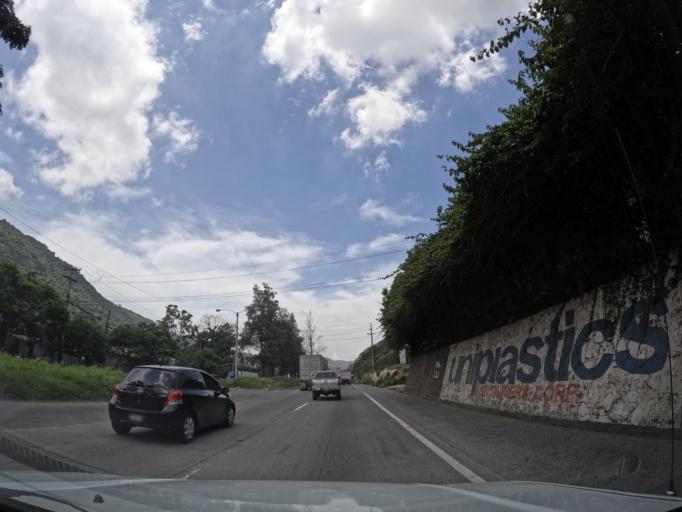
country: GT
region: Escuintla
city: San Vicente Pacaya
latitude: 14.4416
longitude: -90.6499
